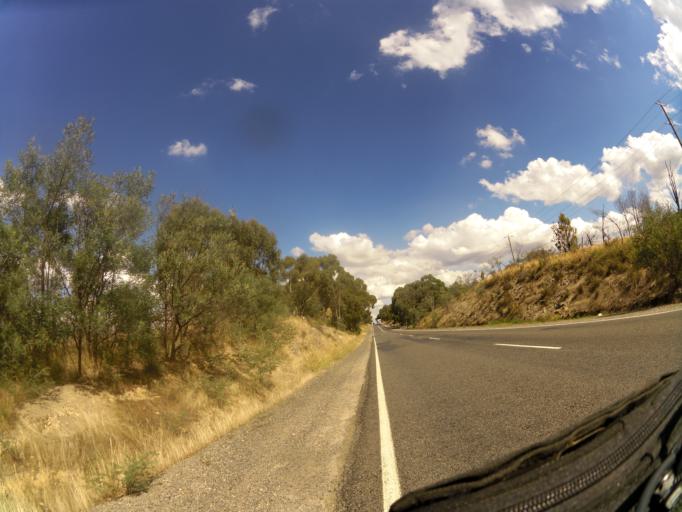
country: AU
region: Victoria
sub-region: Mansfield
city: Mansfield
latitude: -36.8836
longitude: 145.9946
